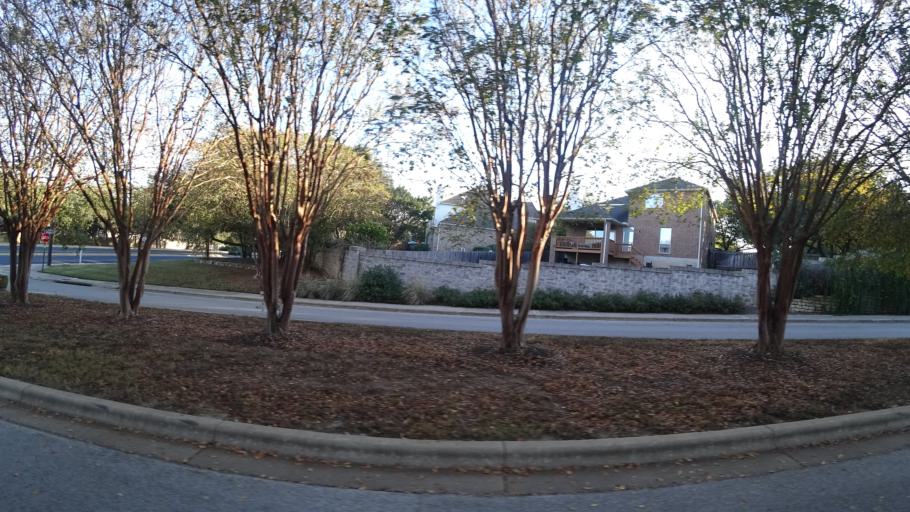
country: US
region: Texas
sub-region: Travis County
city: Hudson Bend
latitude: 30.3761
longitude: -97.8921
